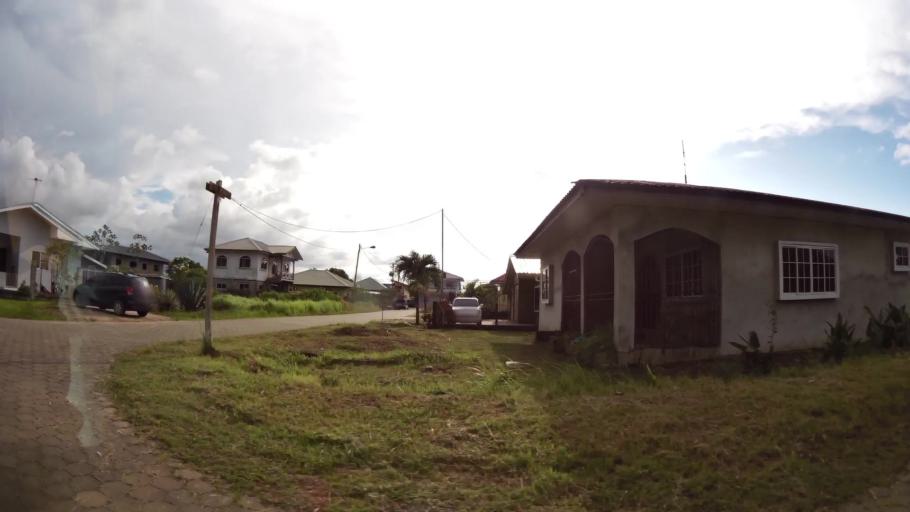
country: SR
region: Paramaribo
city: Paramaribo
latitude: 5.8492
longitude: -55.1772
